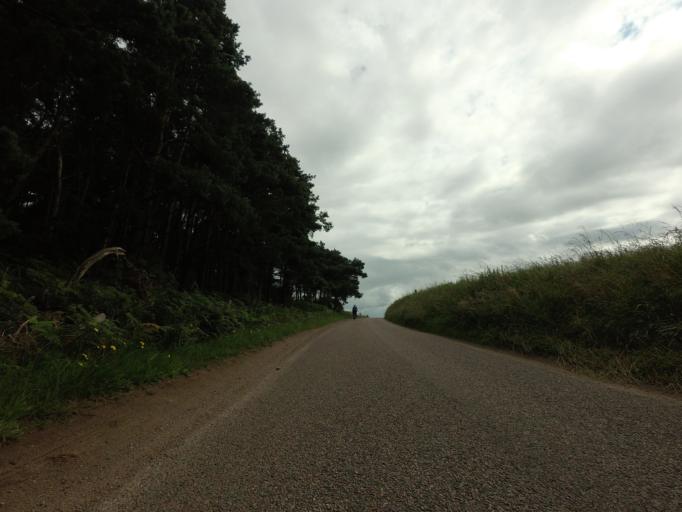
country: GB
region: Scotland
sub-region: Moray
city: Lhanbryd
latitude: 57.6678
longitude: -3.1596
